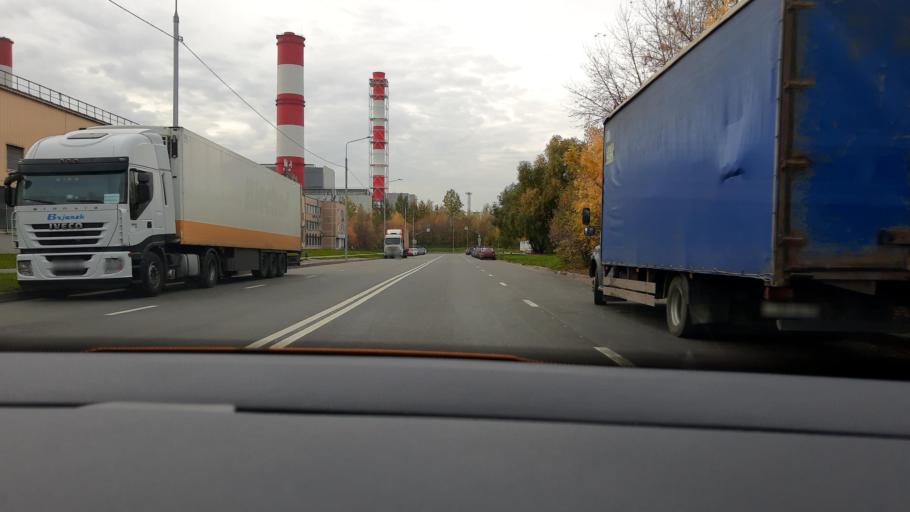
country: RU
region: Moskovskaya
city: Biryulevo Zapadnoye
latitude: 55.5836
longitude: 37.6265
